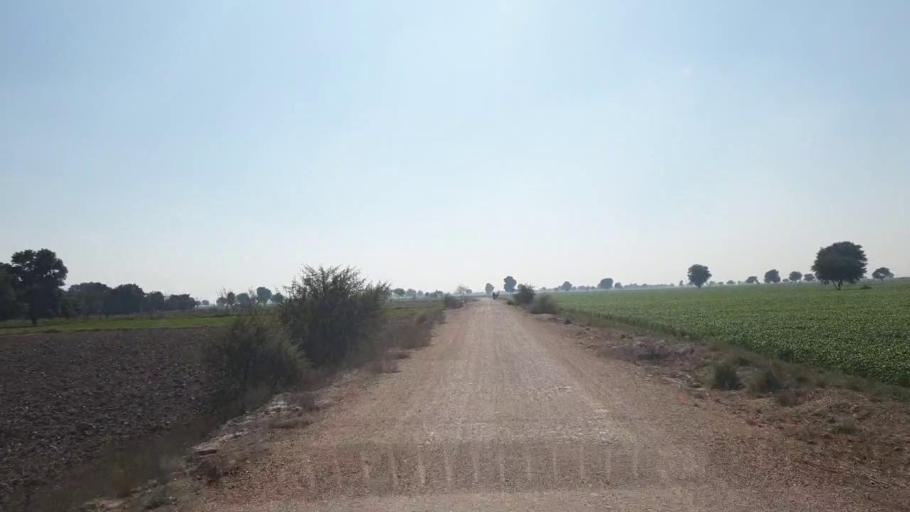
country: PK
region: Sindh
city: Shahpur Chakar
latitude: 26.1061
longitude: 68.6308
